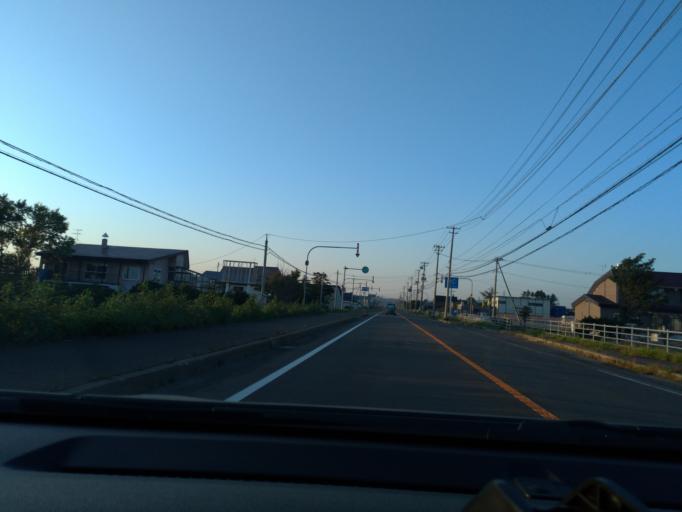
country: JP
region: Hokkaido
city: Tobetsu
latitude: 43.2016
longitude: 141.5214
